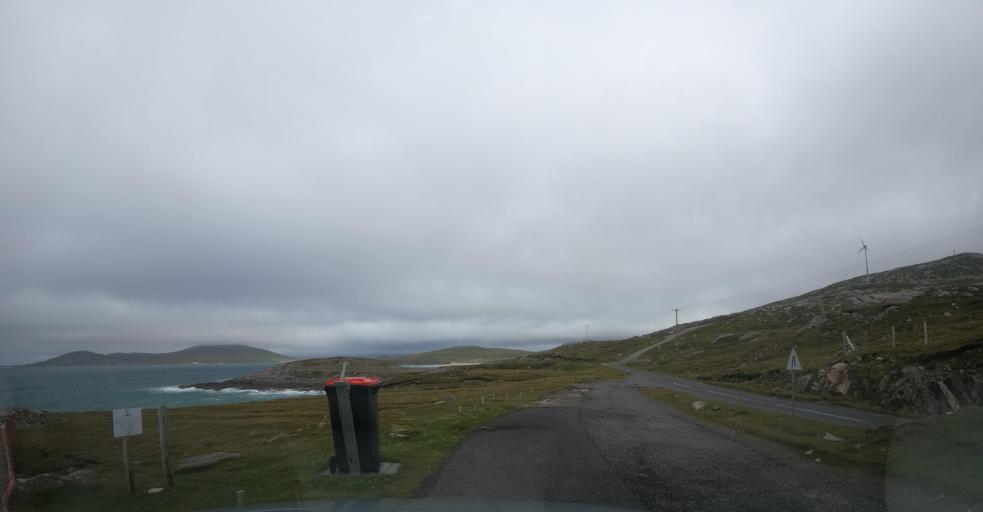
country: GB
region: Scotland
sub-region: Eilean Siar
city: Harris
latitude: 57.8547
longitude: -7.0001
